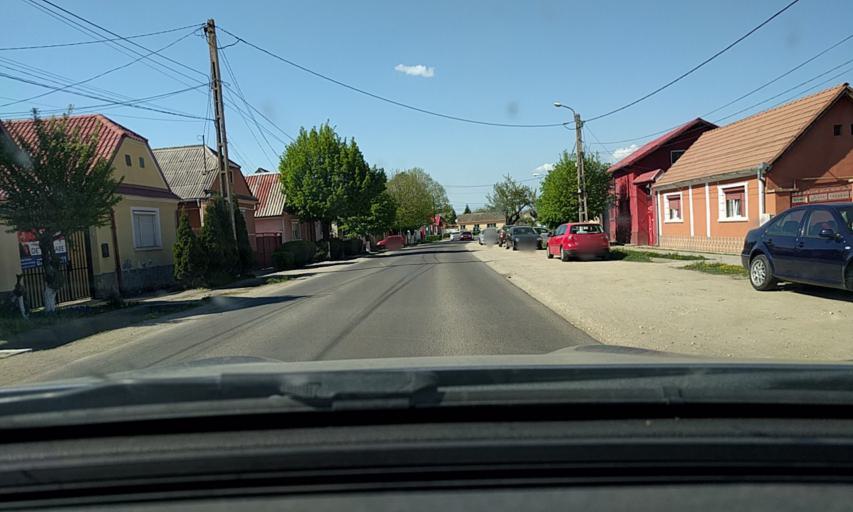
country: RO
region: Brasov
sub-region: Comuna Harman
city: Harman
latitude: 45.7105
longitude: 25.6849
